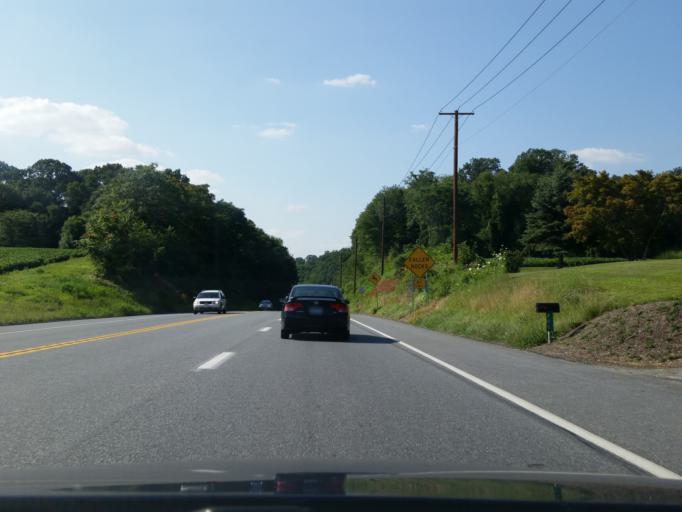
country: US
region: Pennsylvania
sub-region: Lancaster County
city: Columbia
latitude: 40.0470
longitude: -76.5145
